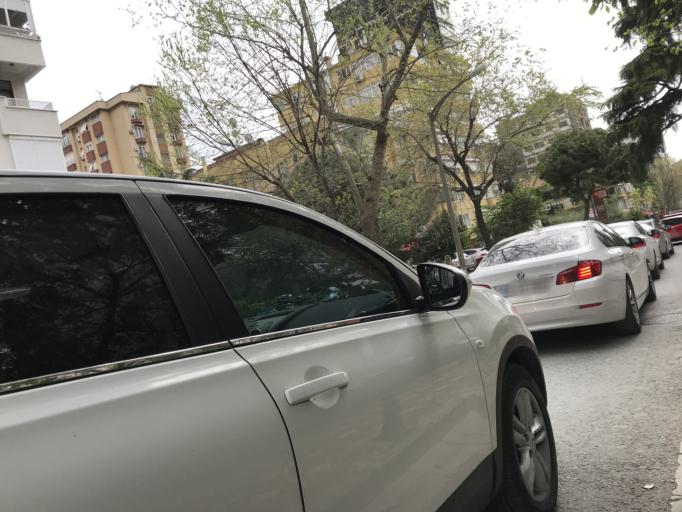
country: TR
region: Istanbul
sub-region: Atasehir
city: Atasehir
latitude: 40.9735
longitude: 29.0626
